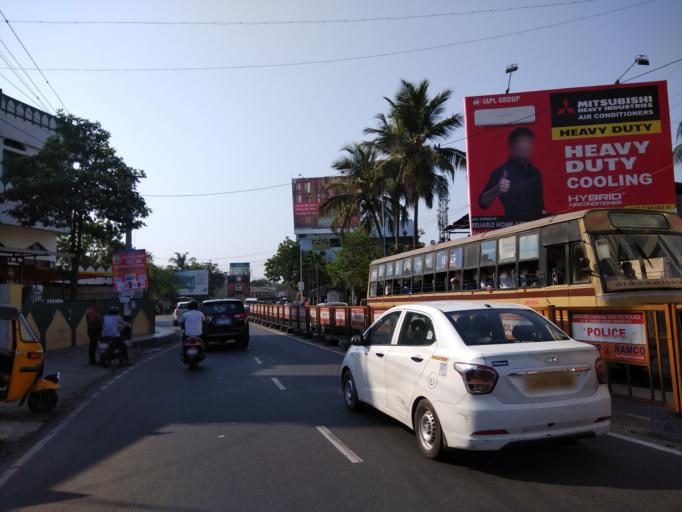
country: IN
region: Tamil Nadu
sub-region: Kancheepuram
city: Saint Thomas Mount
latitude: 13.0089
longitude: 80.1961
